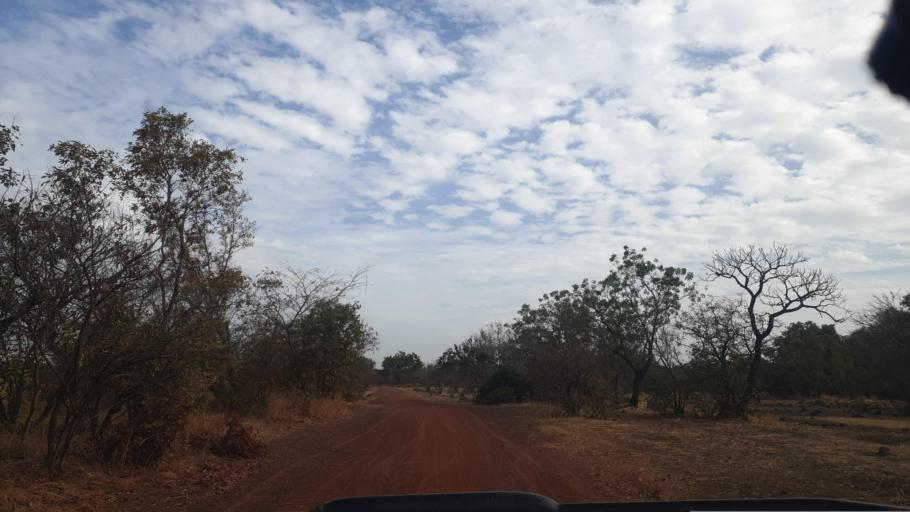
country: ML
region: Sikasso
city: Yanfolila
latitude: 11.3959
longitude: -8.0193
